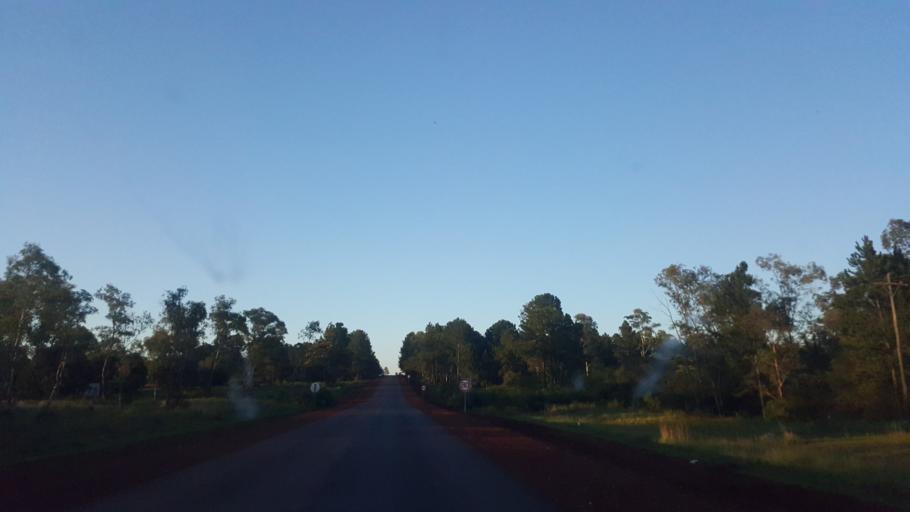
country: AR
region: Corrientes
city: Santo Tome
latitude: -28.5167
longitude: -56.0581
